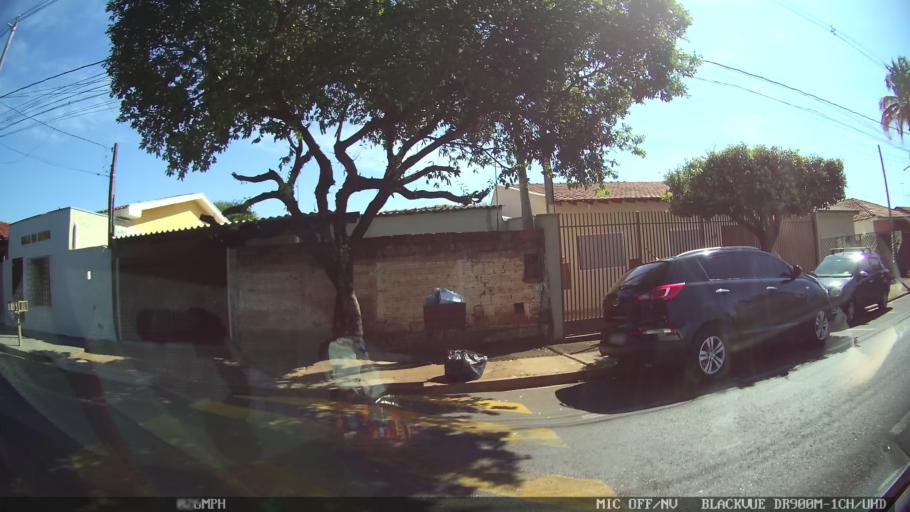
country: BR
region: Sao Paulo
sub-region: Sao Jose Do Rio Preto
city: Sao Jose do Rio Preto
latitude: -20.7717
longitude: -49.4175
